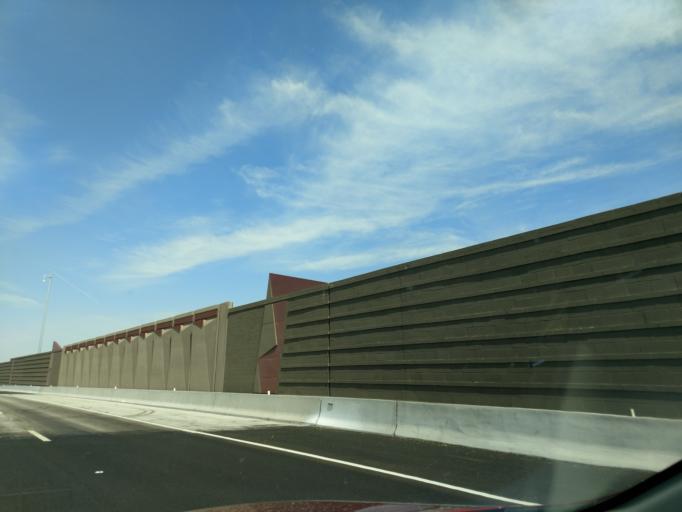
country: US
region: Arizona
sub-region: Maricopa County
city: Guadalupe
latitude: 33.2908
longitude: -111.9960
